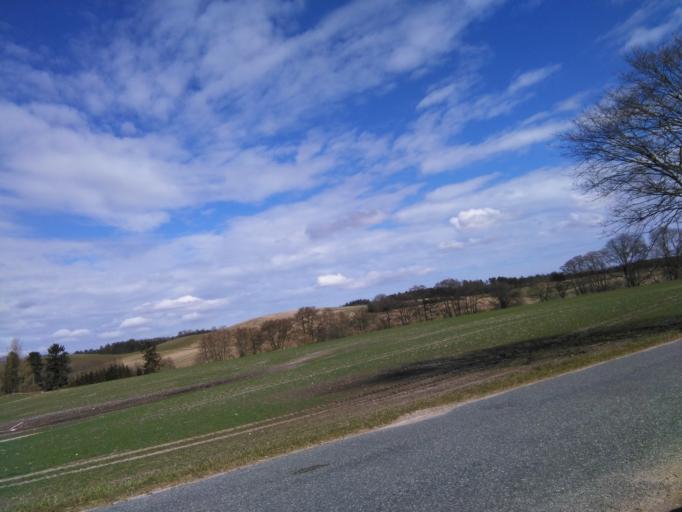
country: DK
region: Central Jutland
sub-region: Odder Kommune
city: Odder
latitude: 55.8908
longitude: 10.0284
